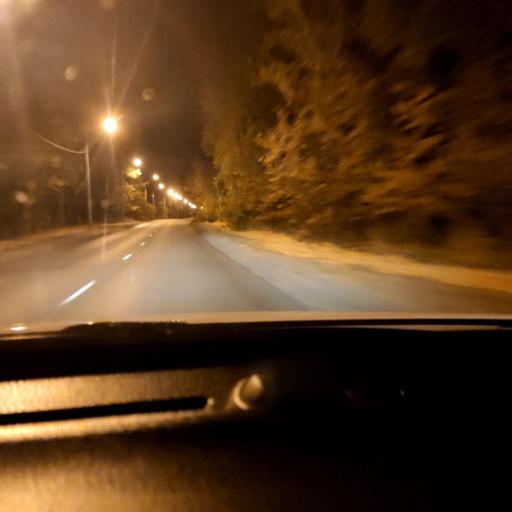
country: RU
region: Voronezj
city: Somovo
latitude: 51.7219
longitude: 39.3203
